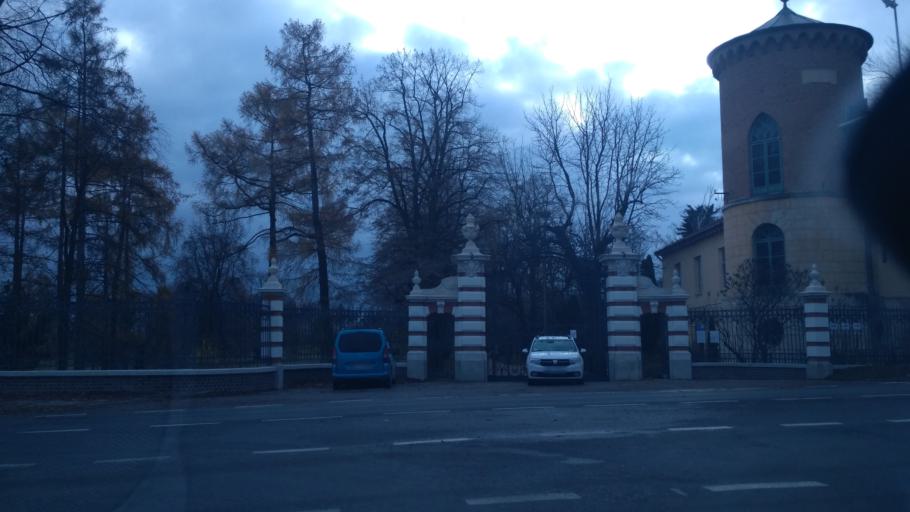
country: PL
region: Subcarpathian Voivodeship
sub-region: Powiat lancucki
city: Lancut
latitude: 50.0707
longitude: 22.2375
